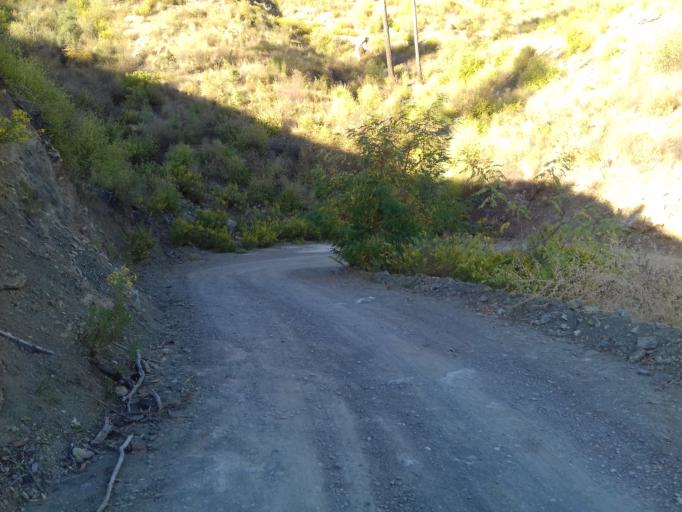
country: TR
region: Mugla
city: Yaniklar
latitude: 36.7950
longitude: 29.0252
